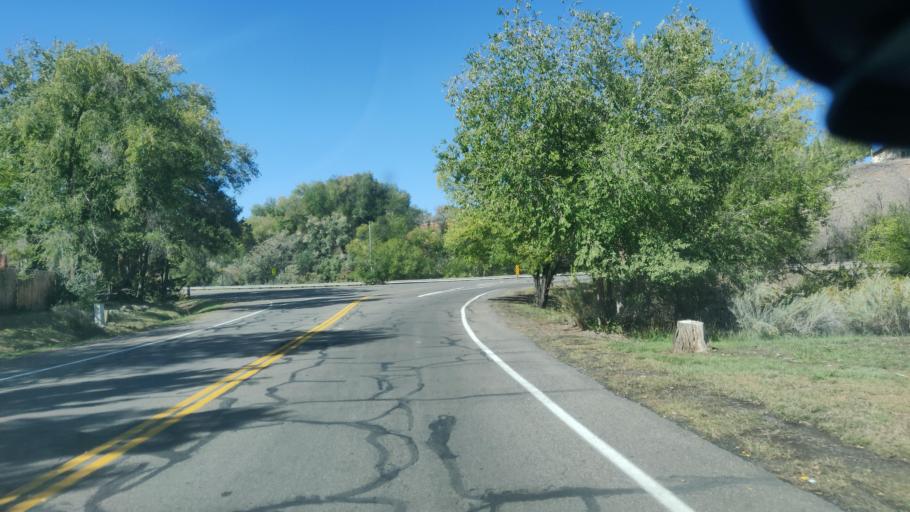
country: US
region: Colorado
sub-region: Mesa County
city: Redlands
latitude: 39.0829
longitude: -108.6296
